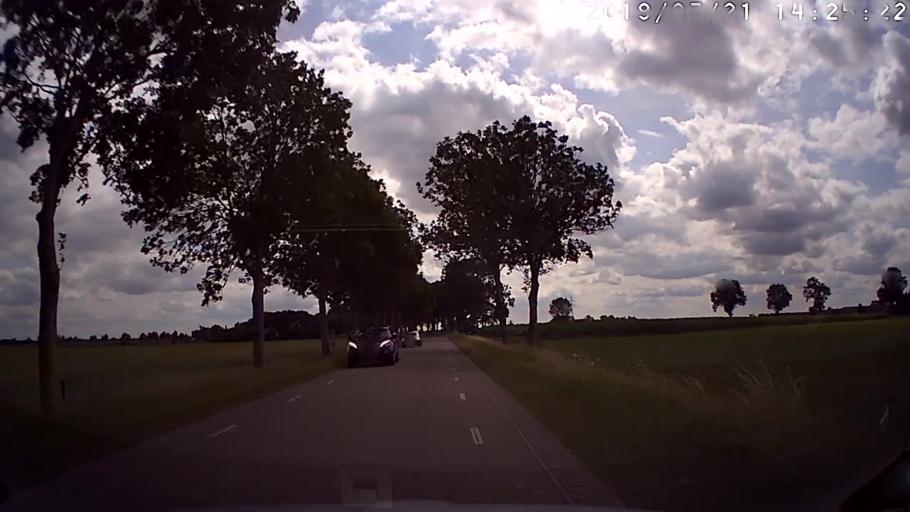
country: NL
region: Overijssel
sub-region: Gemeente Raalte
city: Heino
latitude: 52.4454
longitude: 6.1877
